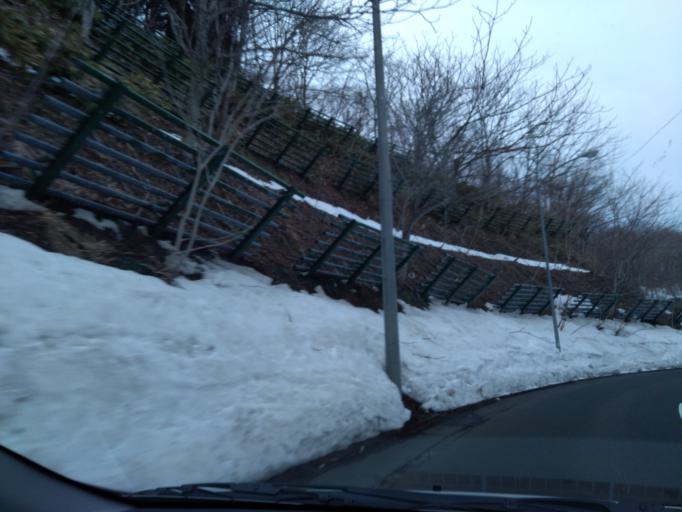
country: JP
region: Iwate
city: Kitakami
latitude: 39.2358
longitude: 140.9357
